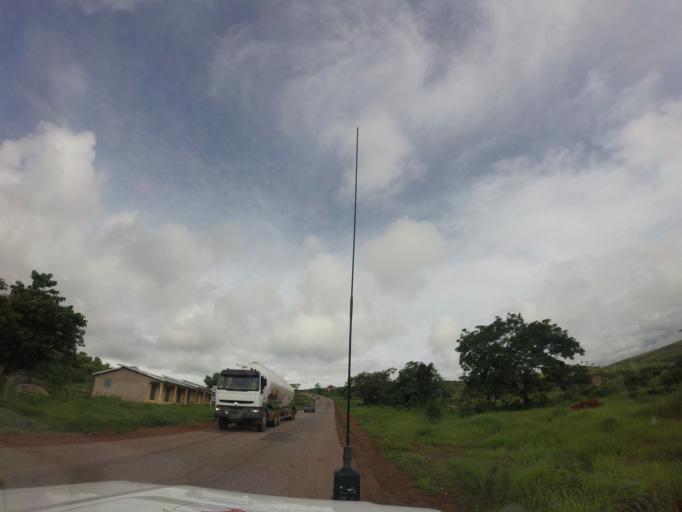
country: GN
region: Kindia
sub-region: Coyah
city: Coyah
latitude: 9.8336
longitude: -13.2320
